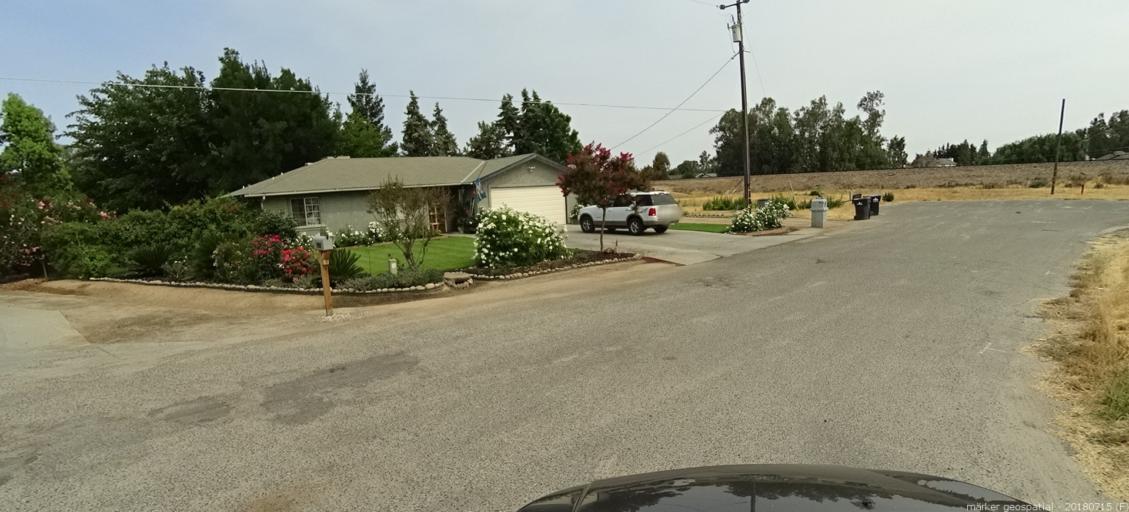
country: US
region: California
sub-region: Madera County
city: Madera Acres
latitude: 37.0193
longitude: -120.0728
